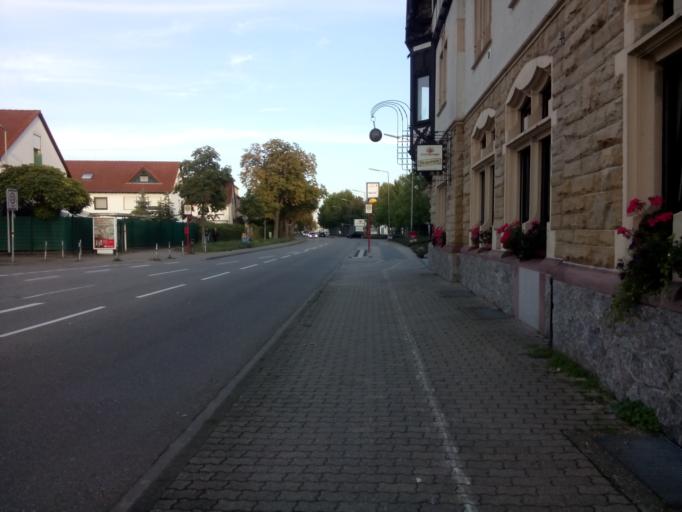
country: DE
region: Baden-Wuerttemberg
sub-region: Karlsruhe Region
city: Karlsruhe
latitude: 49.0031
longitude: 8.3558
